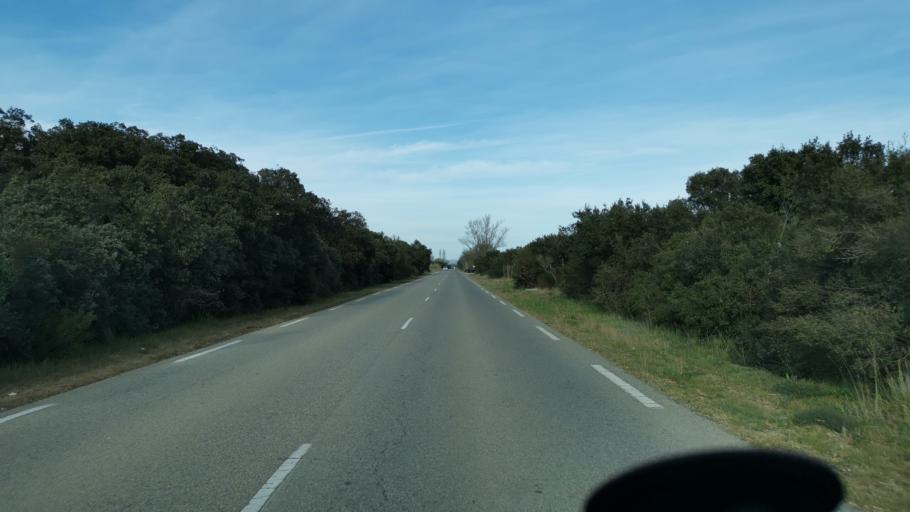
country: FR
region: Provence-Alpes-Cote d'Azur
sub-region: Departement des Bouches-du-Rhone
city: Saint-Martin-de-Crau
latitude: 43.5759
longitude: 4.7516
